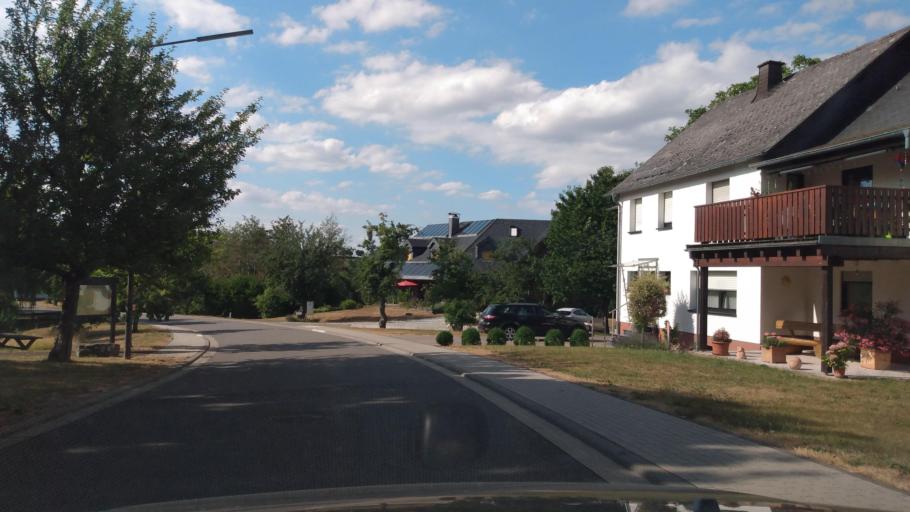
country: DE
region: Rheinland-Pfalz
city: Deuselbach
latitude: 49.7523
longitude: 7.0555
